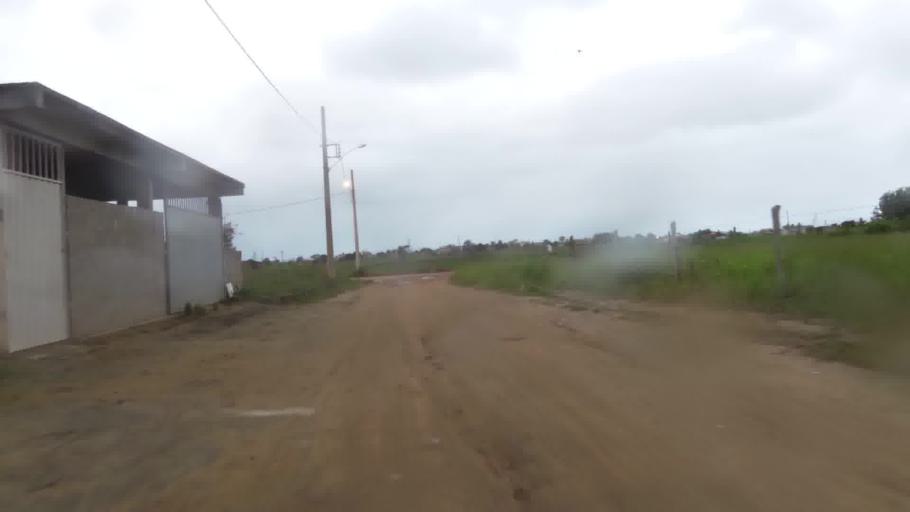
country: BR
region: Espirito Santo
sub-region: Marataizes
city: Marataizes
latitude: -21.0409
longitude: -40.8417
